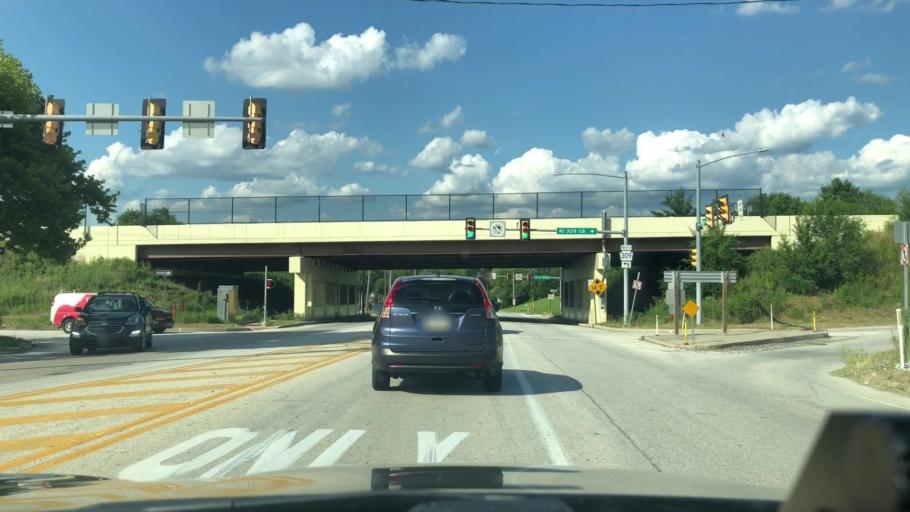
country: US
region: Pennsylvania
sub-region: Montgomery County
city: Flourtown
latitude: 40.1013
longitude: -75.1942
